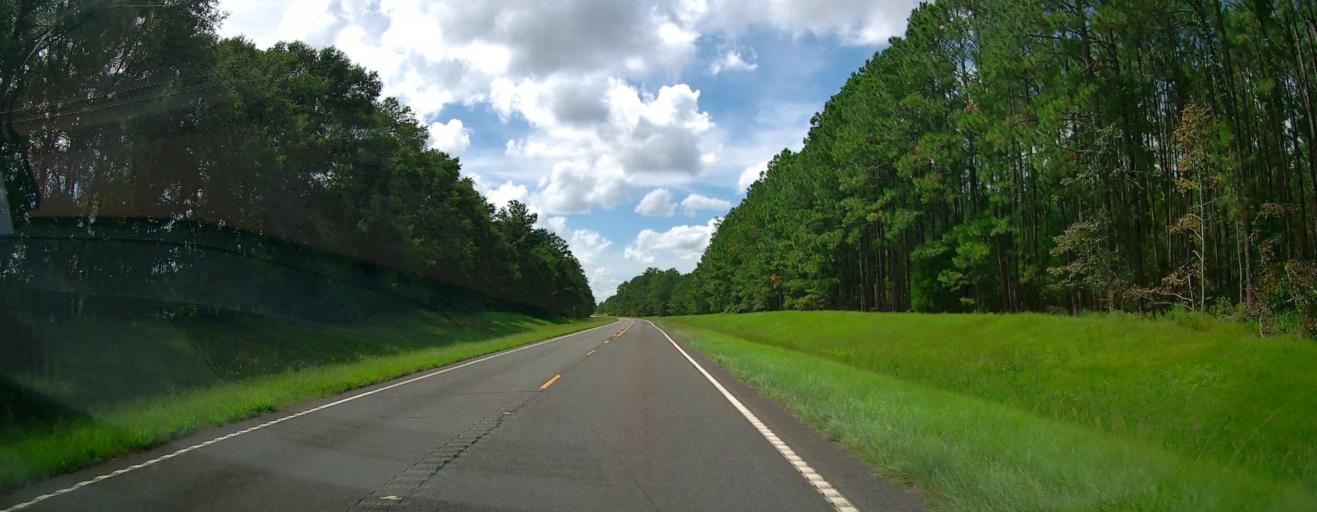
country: US
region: Georgia
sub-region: Macon County
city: Marshallville
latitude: 32.4336
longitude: -84.0426
